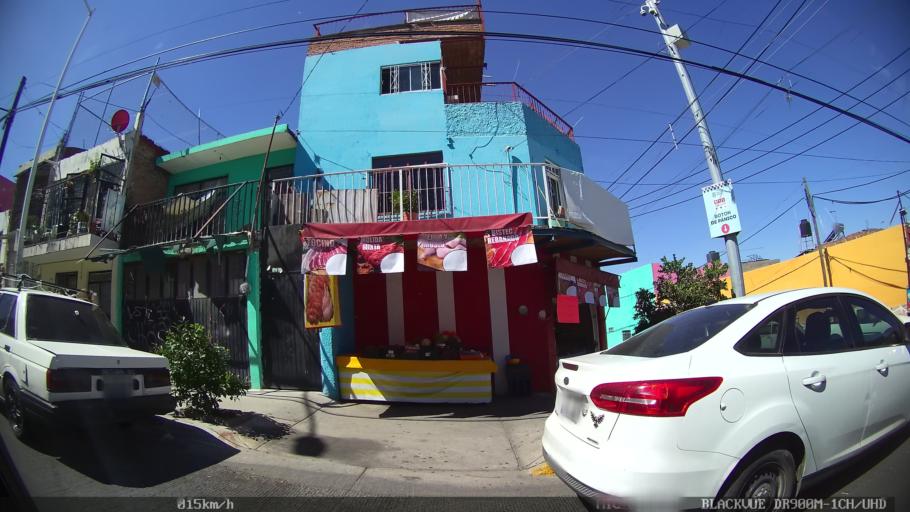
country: MX
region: Jalisco
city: Tlaquepaque
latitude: 20.6949
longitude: -103.2832
